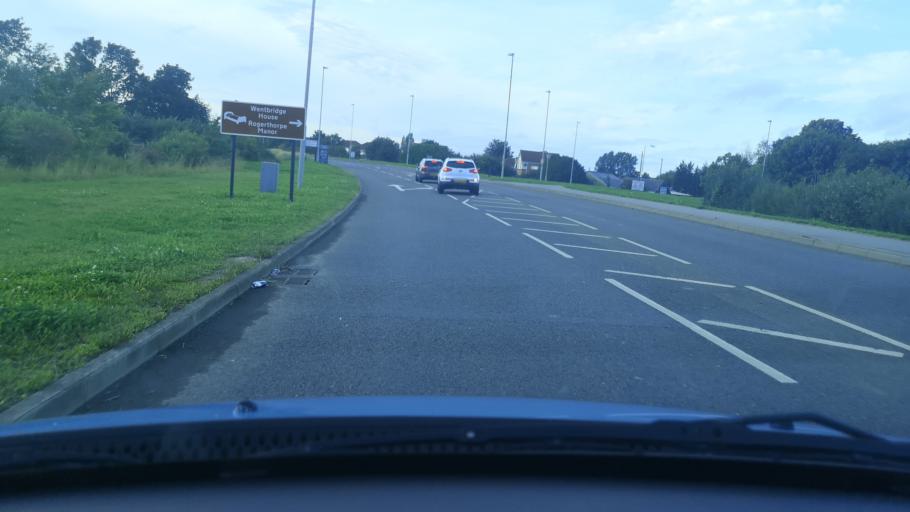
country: GB
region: England
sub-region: City and Borough of Wakefield
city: Upton
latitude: 53.6096
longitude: -1.2877
